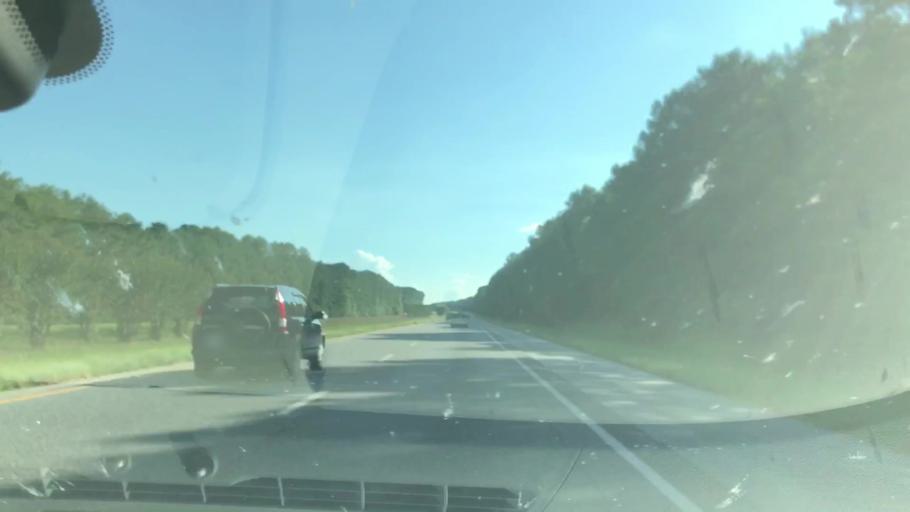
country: US
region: Georgia
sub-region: Harris County
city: Pine Mountain
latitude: 32.8931
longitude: -84.9536
